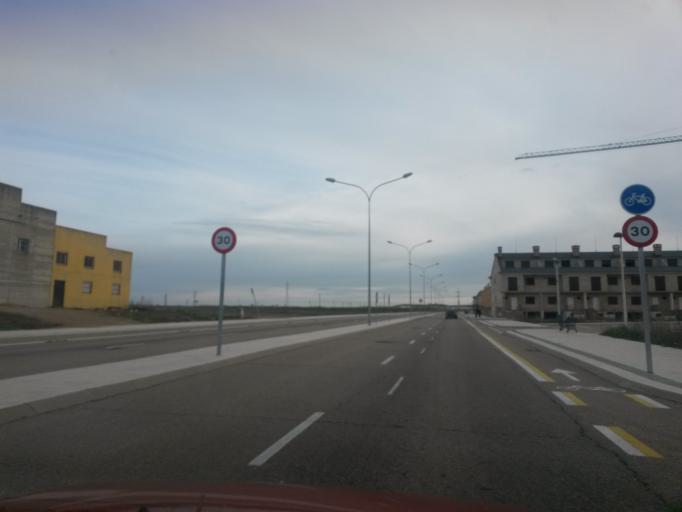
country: ES
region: Castille and Leon
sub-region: Provincia de Salamanca
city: Villares de la Reina
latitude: 41.0079
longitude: -5.6436
